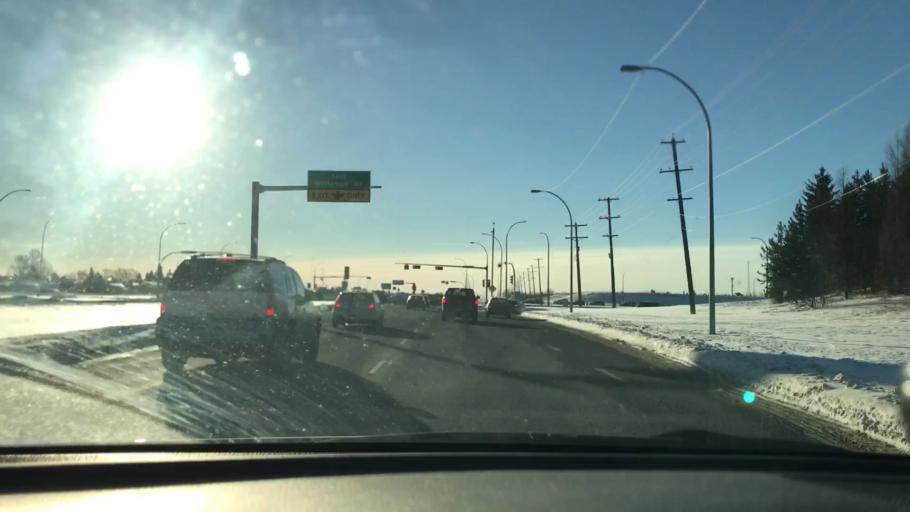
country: CA
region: Alberta
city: Edmonton
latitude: 53.4837
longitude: -113.4693
